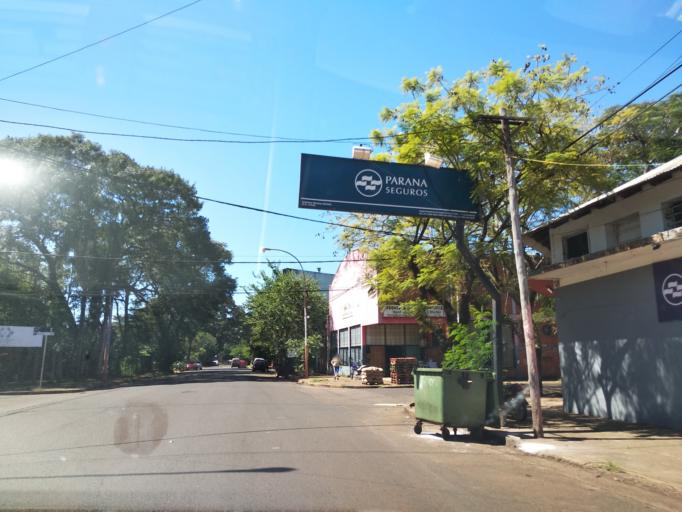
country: AR
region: Misiones
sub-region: Departamento de Iguazu
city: Puerto Iguazu
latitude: -25.5958
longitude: -54.5733
